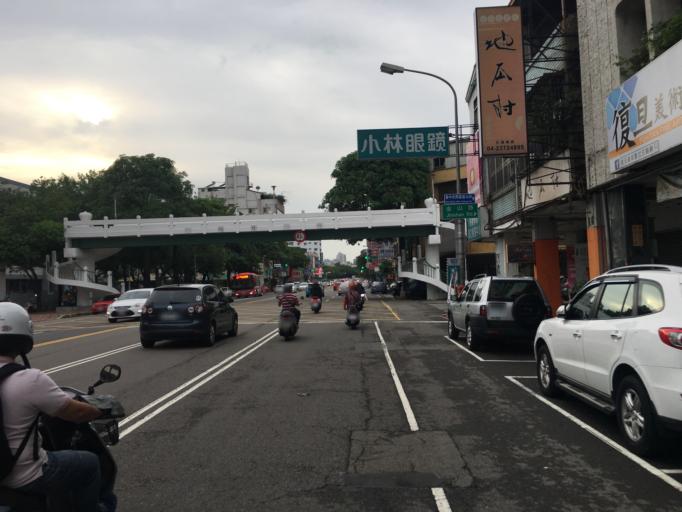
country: TW
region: Taiwan
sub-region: Taichung City
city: Taichung
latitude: 24.1390
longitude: 120.6692
